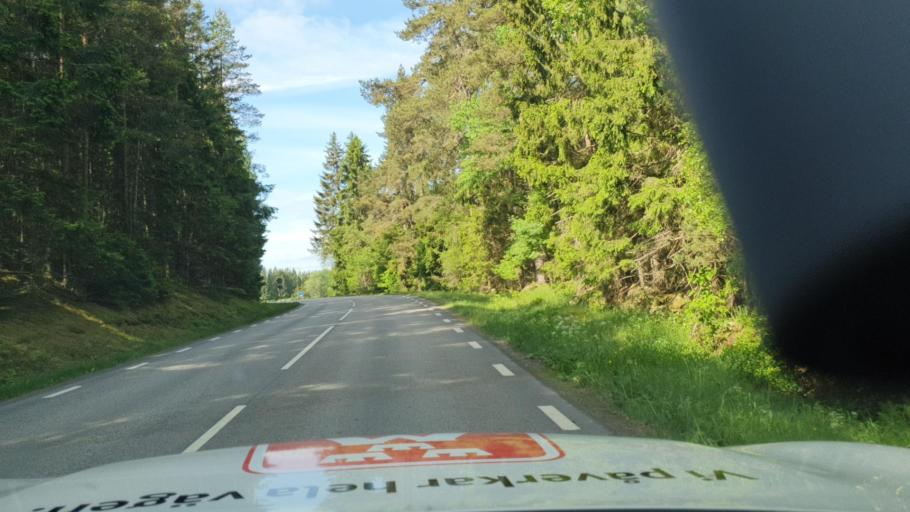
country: SE
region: Vaestra Goetaland
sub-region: Herrljunga Kommun
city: Herrljunga
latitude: 58.0082
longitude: 13.1246
